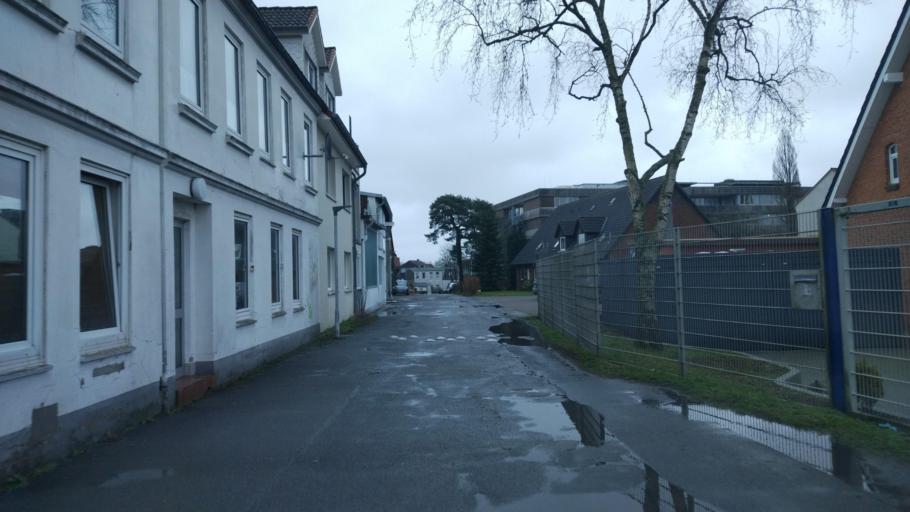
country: DE
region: Schleswig-Holstein
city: Schleswig
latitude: 54.5205
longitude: 9.5596
